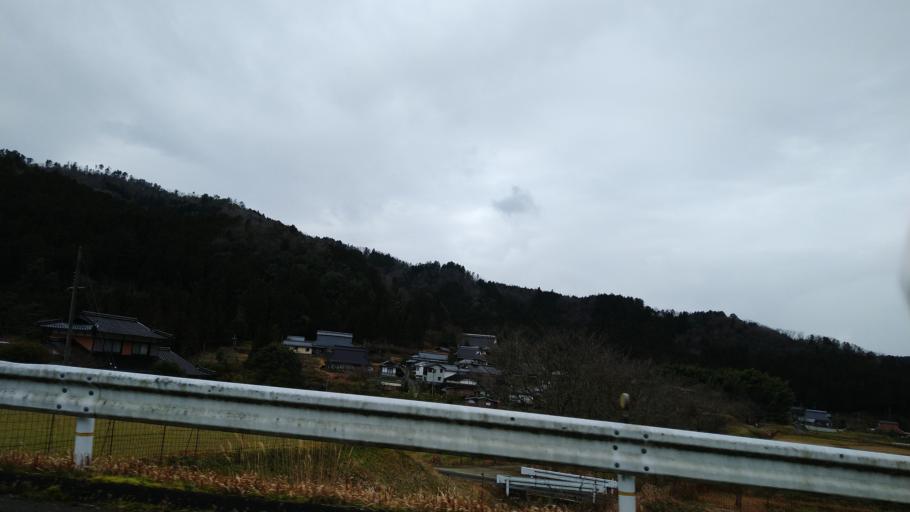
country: JP
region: Kyoto
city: Ayabe
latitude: 35.3285
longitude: 135.3543
